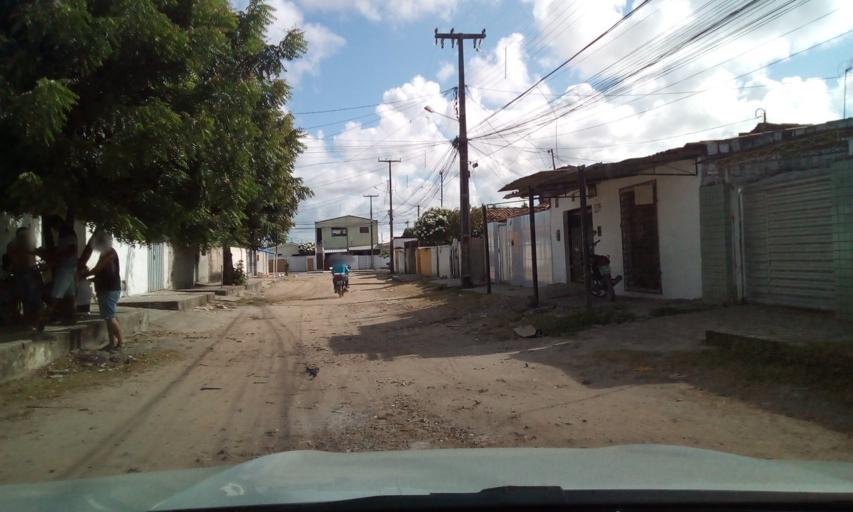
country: BR
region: Paraiba
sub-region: Joao Pessoa
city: Joao Pessoa
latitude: -7.1679
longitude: -34.8348
